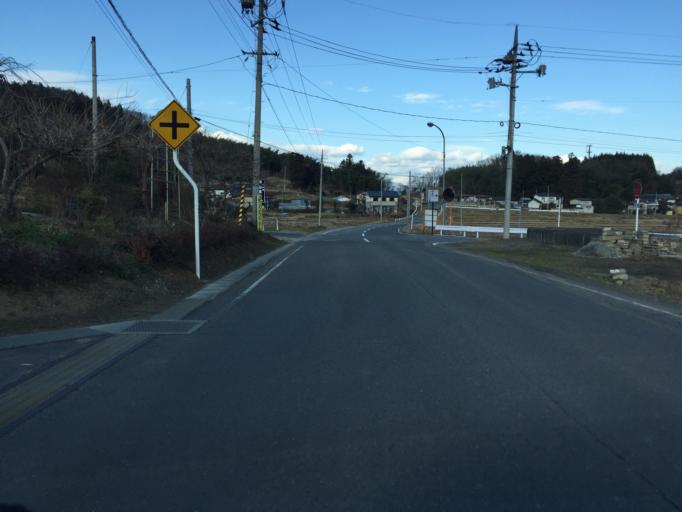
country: JP
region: Fukushima
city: Fukushima-shi
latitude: 37.7199
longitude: 140.4256
